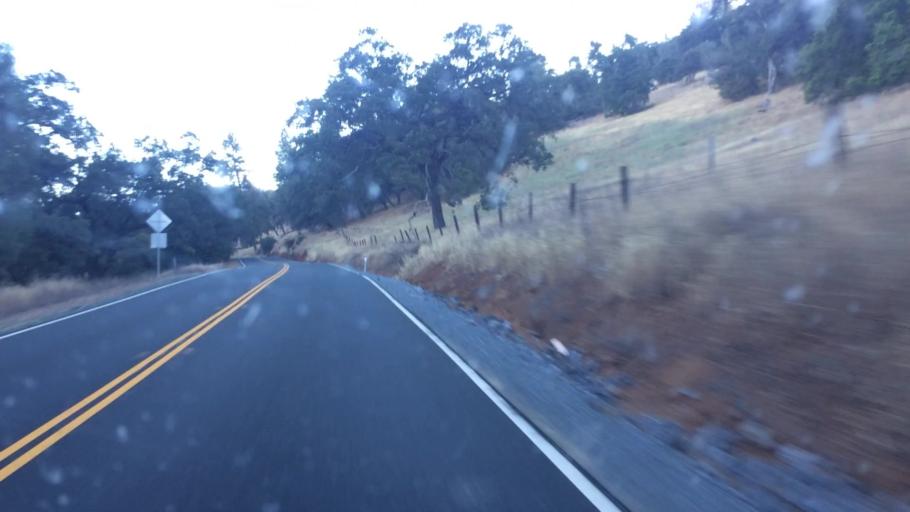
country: US
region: California
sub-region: El Dorado County
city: Deer Park
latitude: 38.6174
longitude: -120.8513
